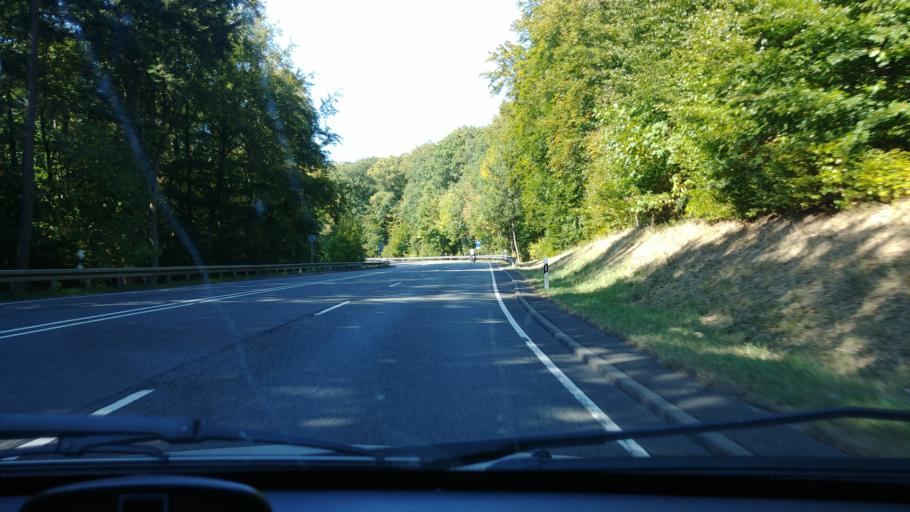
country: DE
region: Hesse
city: Taunusstein
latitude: 50.1211
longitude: 8.1757
